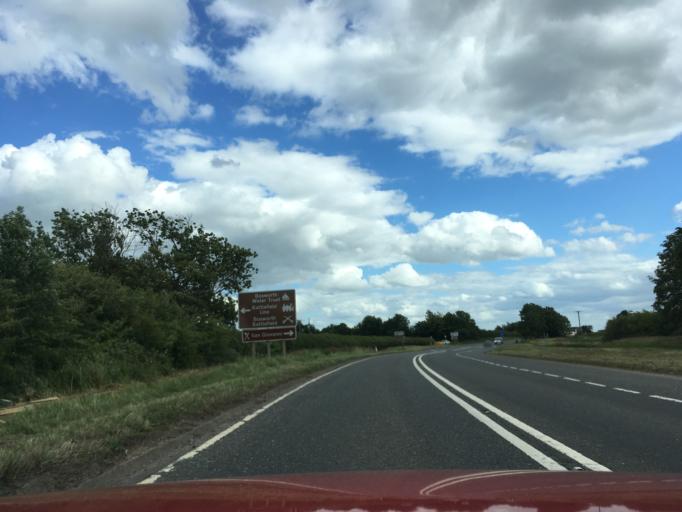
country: GB
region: England
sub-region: Leicestershire
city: Market Bosworth
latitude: 52.6174
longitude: -1.4749
